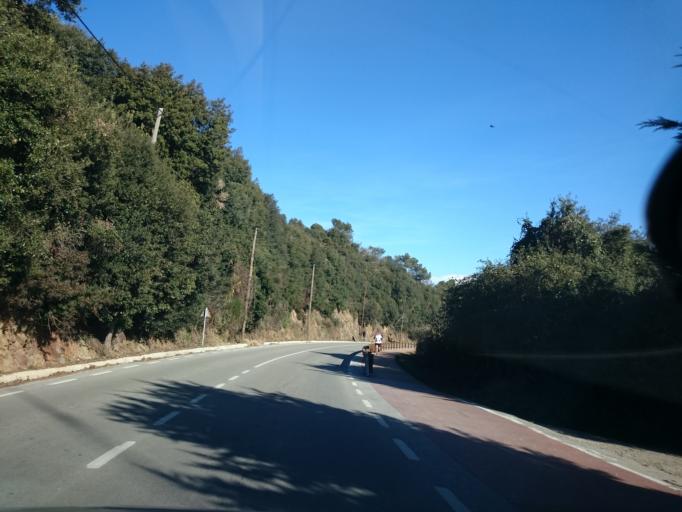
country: ES
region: Catalonia
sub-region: Provincia de Barcelona
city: Sarria-Sant Gervasi
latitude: 41.4238
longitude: 2.1207
